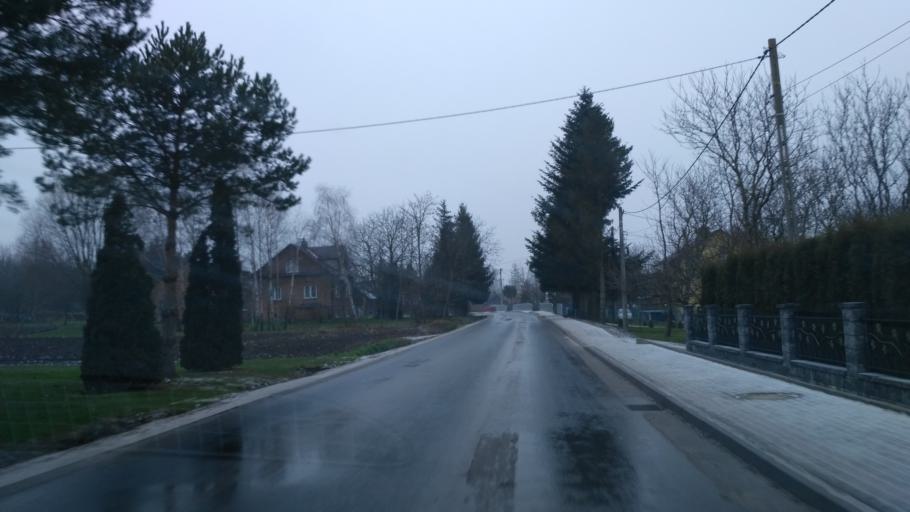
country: PL
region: Subcarpathian Voivodeship
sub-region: Powiat przeworski
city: Kanczuga
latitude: 50.0173
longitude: 22.4033
